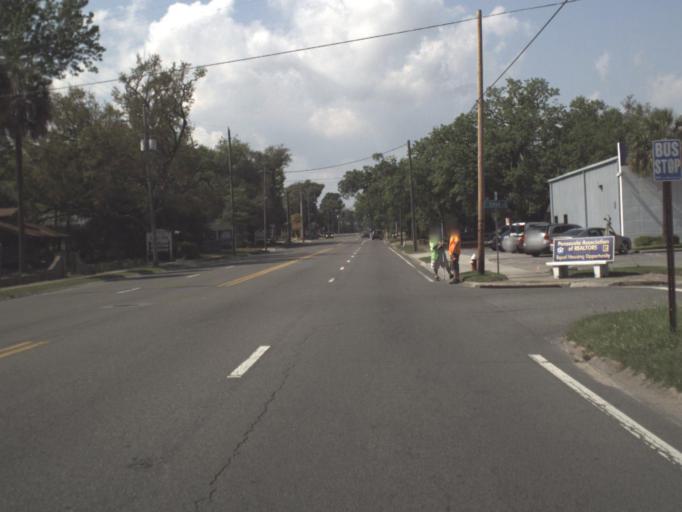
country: US
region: Florida
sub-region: Escambia County
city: Pensacola
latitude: 30.4276
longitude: -87.2081
